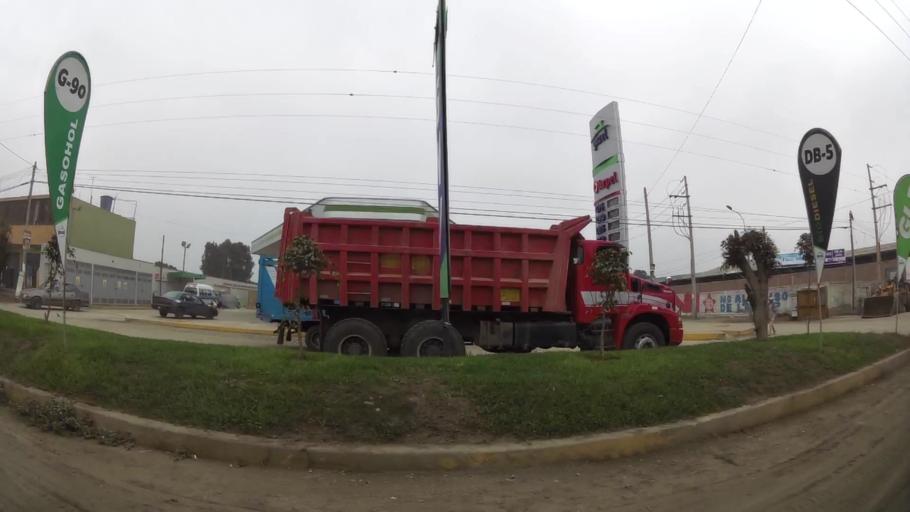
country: PE
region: Lima
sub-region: Lima
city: Punta Hermosa
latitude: -12.2596
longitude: -76.8854
